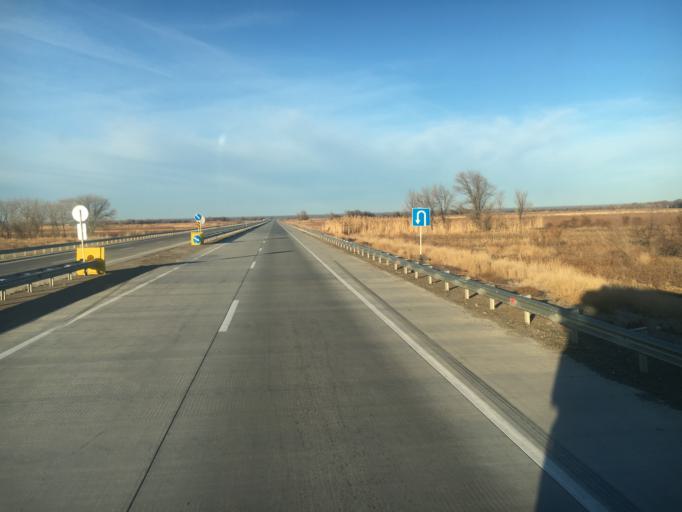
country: KZ
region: Ongtustik Qazaqstan
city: Turkestan
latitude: 43.1562
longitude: 68.5610
